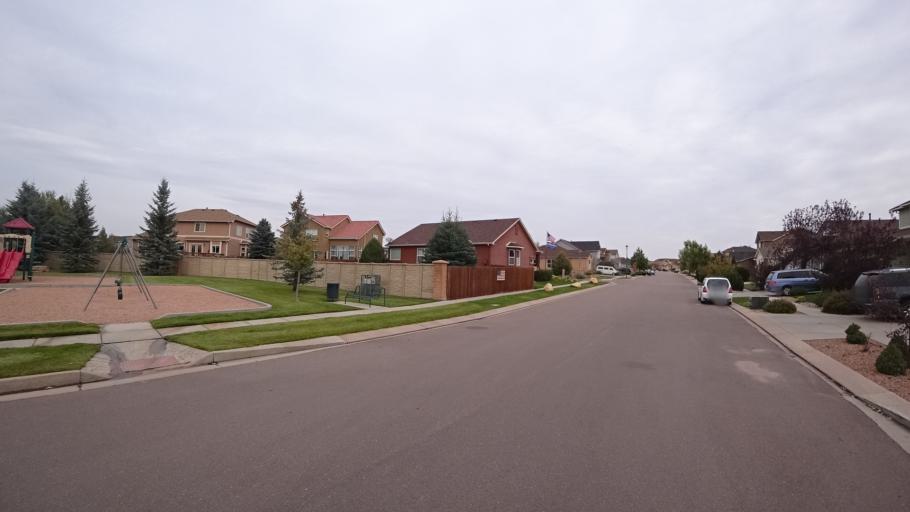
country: US
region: Colorado
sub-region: El Paso County
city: Cimarron Hills
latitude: 38.9186
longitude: -104.6894
